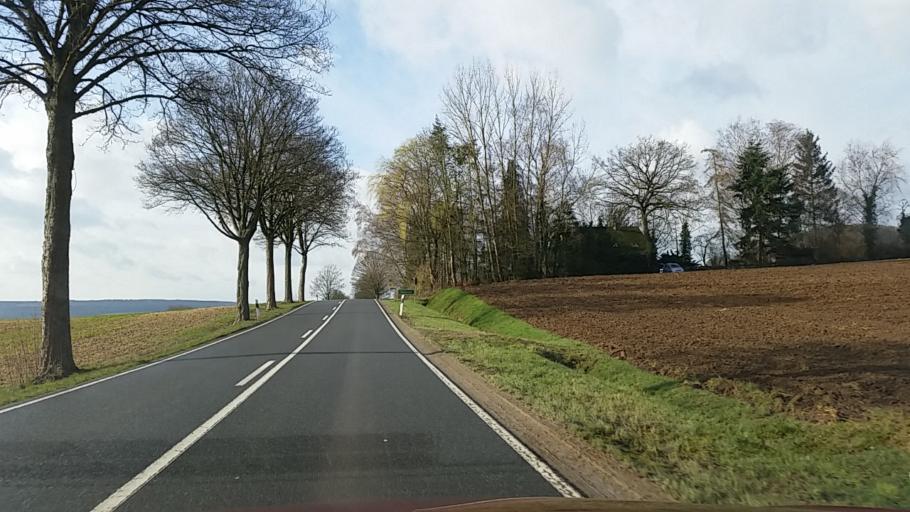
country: DE
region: Lower Saxony
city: Kalefeld
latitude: 51.8150
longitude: 10.1009
